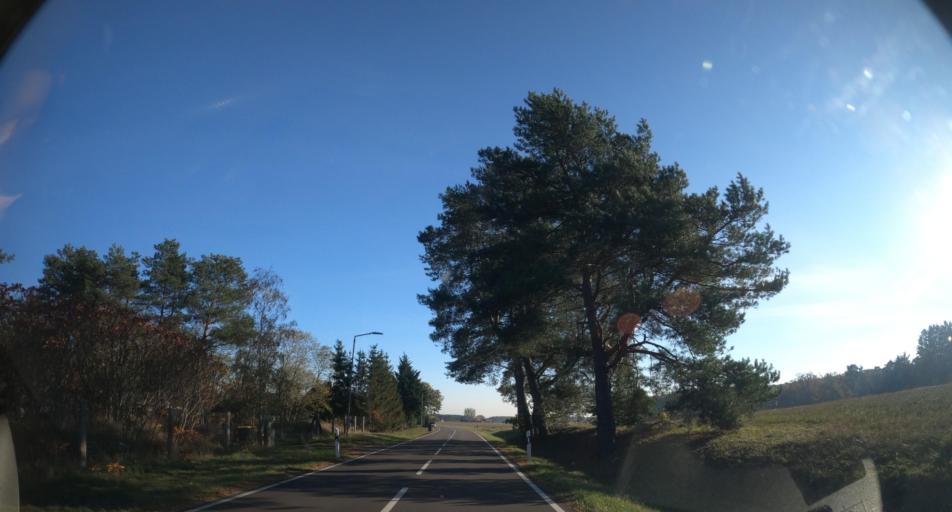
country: DE
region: Mecklenburg-Vorpommern
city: Ahlbeck
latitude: 53.6375
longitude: 14.2156
